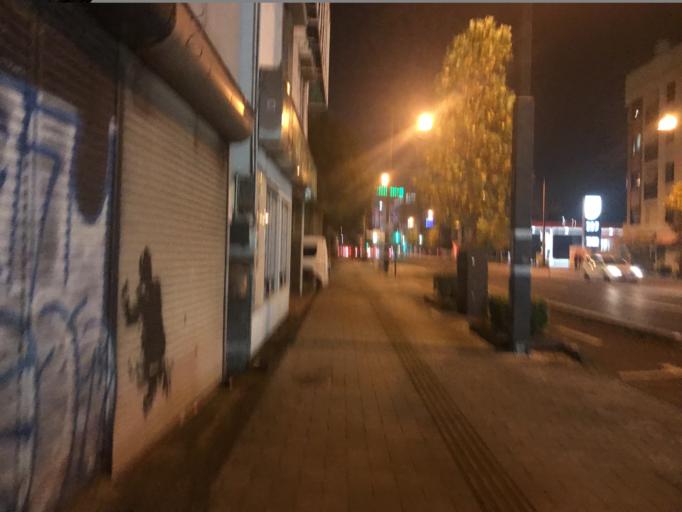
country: JP
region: Okayama
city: Okayama-shi
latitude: 34.6744
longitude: 133.9202
